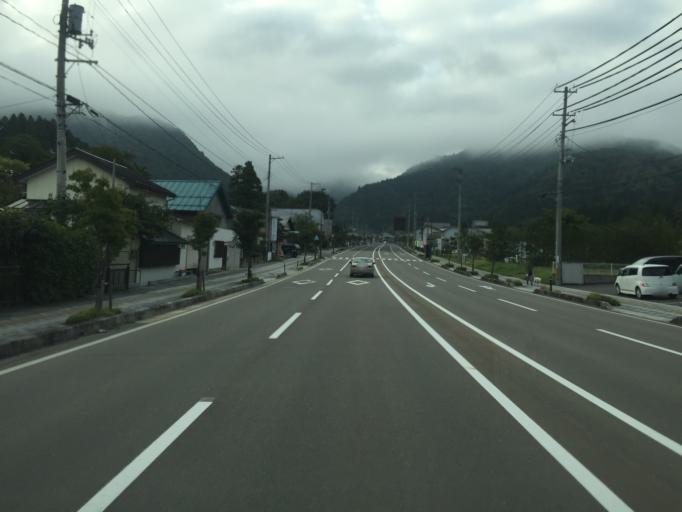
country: JP
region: Fukushima
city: Kitakata
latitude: 37.4874
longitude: 139.9507
